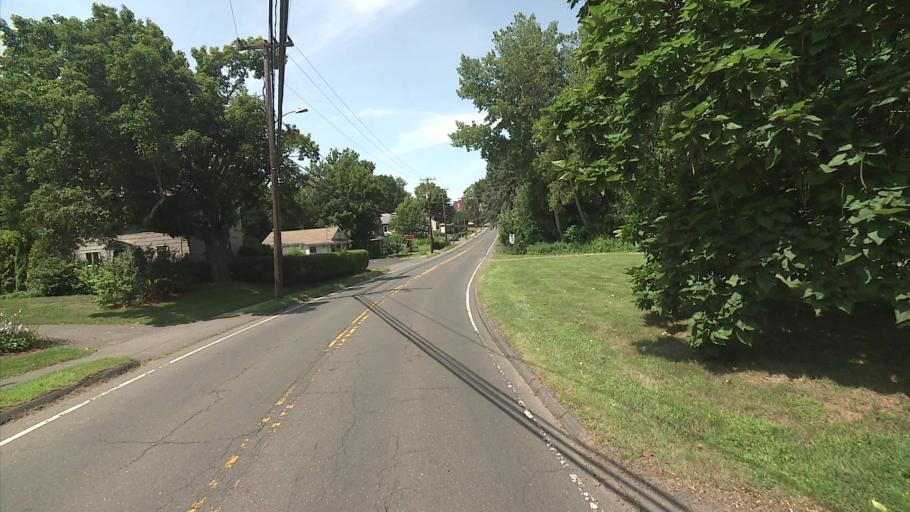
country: US
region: Connecticut
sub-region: Hartford County
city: Kensington
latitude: 41.6312
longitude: -72.7739
